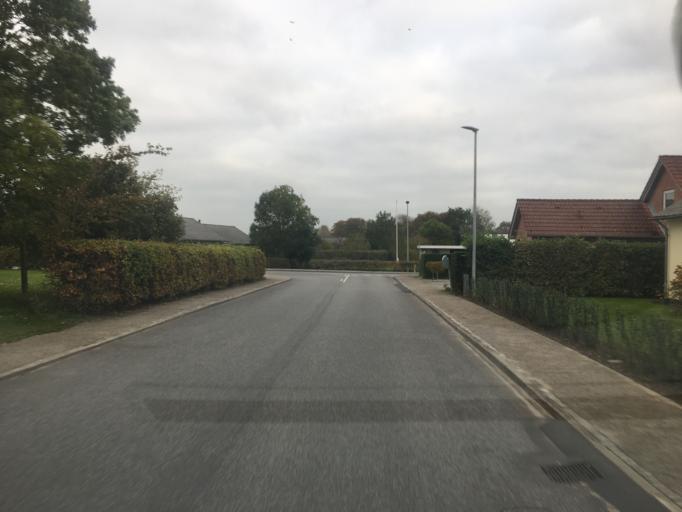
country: DK
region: South Denmark
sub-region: Tonder Kommune
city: Tonder
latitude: 54.9783
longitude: 8.8726
